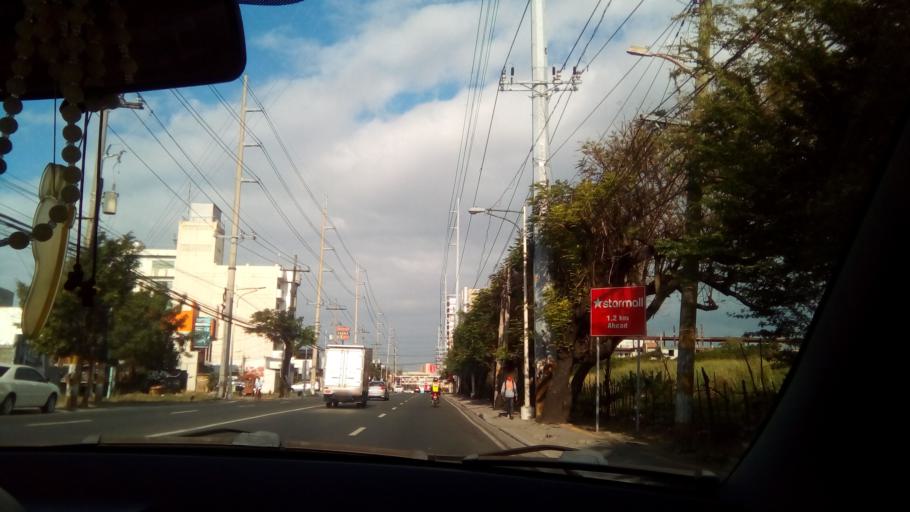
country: PH
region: Calabarzon
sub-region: Province of Rizal
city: Las Pinas
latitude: 14.4470
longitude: 120.9878
